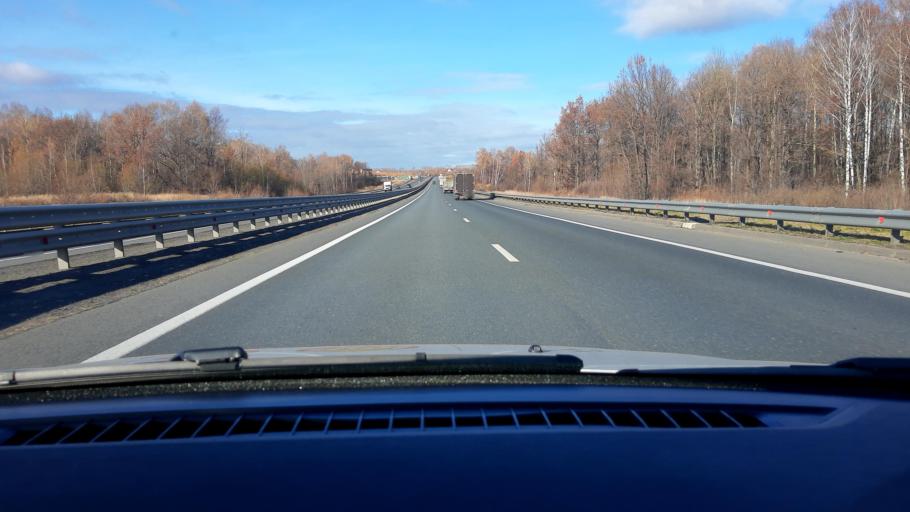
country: RU
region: Nizjnij Novgorod
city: Burevestnik
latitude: 56.1382
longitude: 43.7657
